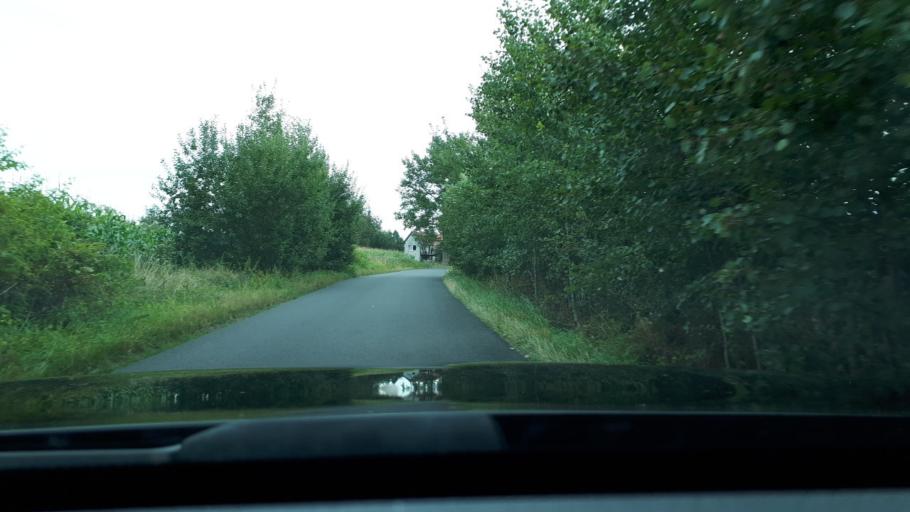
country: PL
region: Lower Silesian Voivodeship
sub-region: Powiat lubanski
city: Olszyna
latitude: 51.0369
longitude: 15.3449
